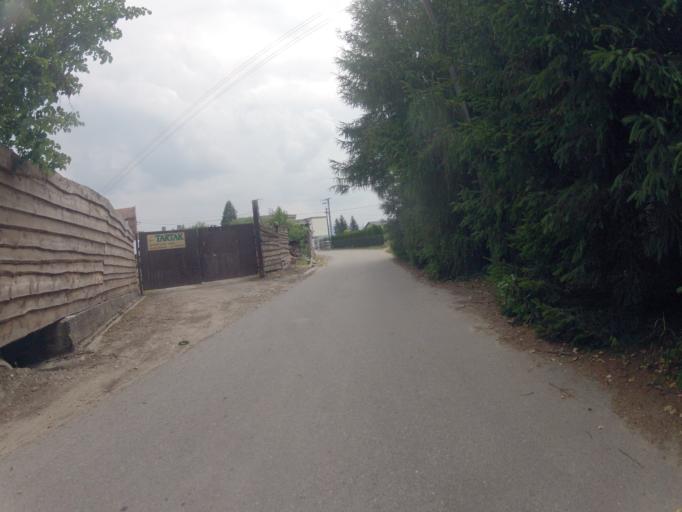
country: PL
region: Lesser Poland Voivodeship
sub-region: Powiat nowosadecki
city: Stary Sacz
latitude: 49.5580
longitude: 20.6604
